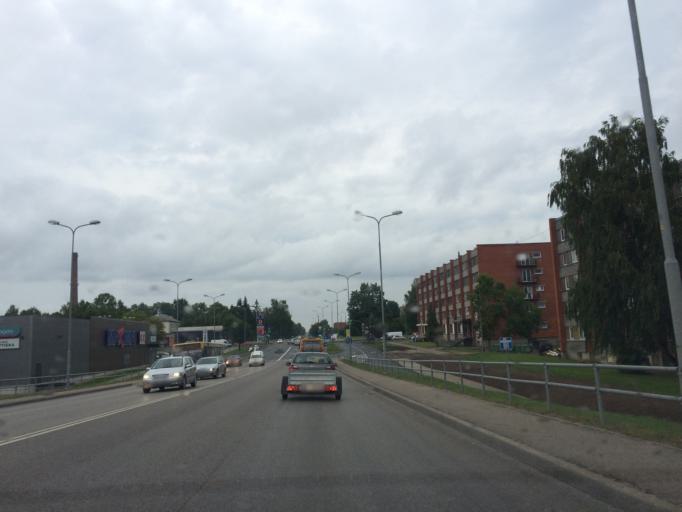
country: LV
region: Rezekne
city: Rezekne
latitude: 56.5223
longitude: 27.3405
